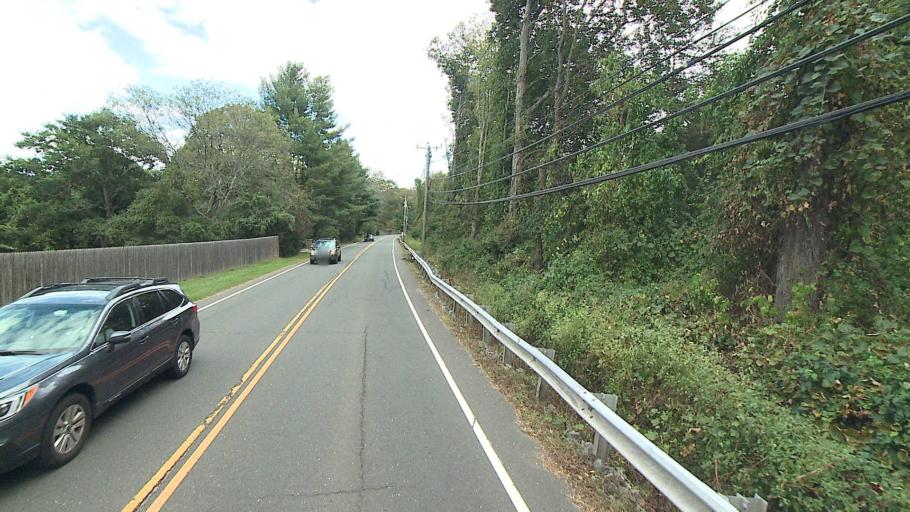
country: US
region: Connecticut
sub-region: Fairfield County
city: Wilton
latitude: 41.2028
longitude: -73.4494
